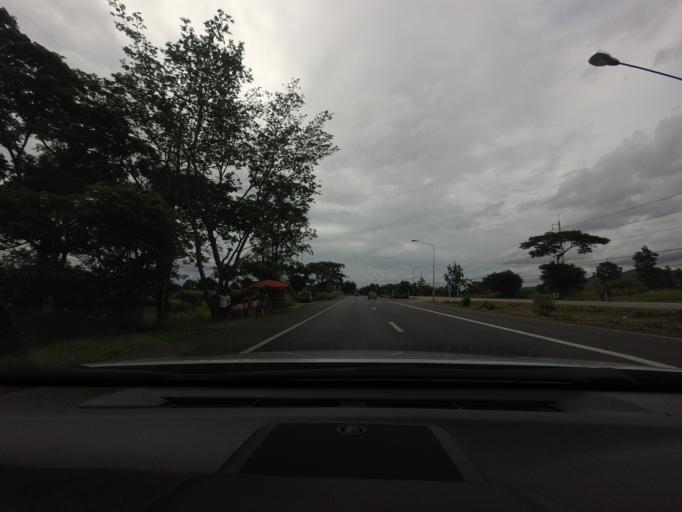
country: TH
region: Prachuap Khiri Khan
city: Hua Hin
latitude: 12.5973
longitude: 99.8630
